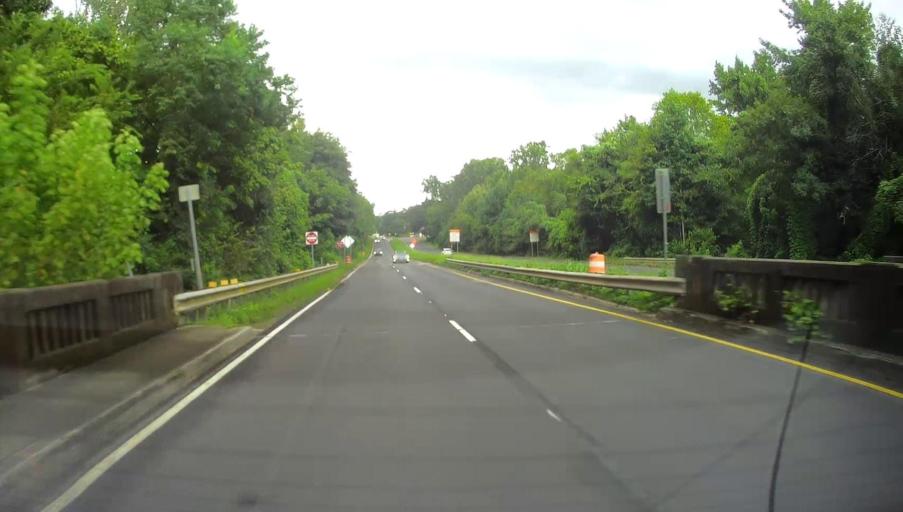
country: US
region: Georgia
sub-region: Bibb County
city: Macon
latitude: 32.8463
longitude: -83.5959
